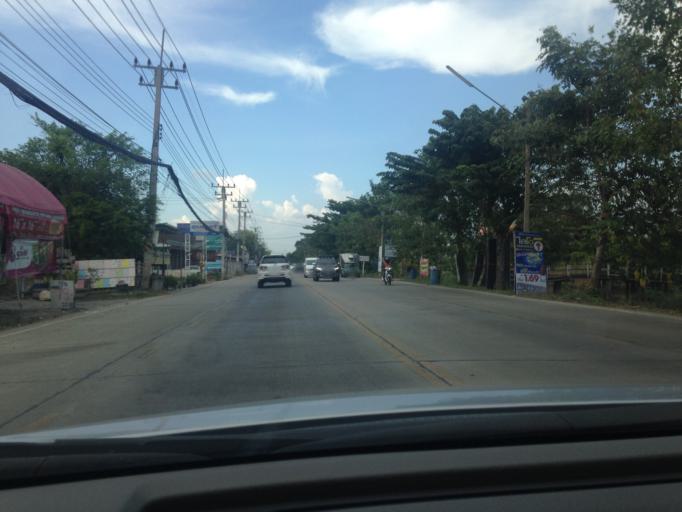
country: TH
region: Pathum Thani
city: Khlong Luang
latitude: 14.0613
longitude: 100.6635
